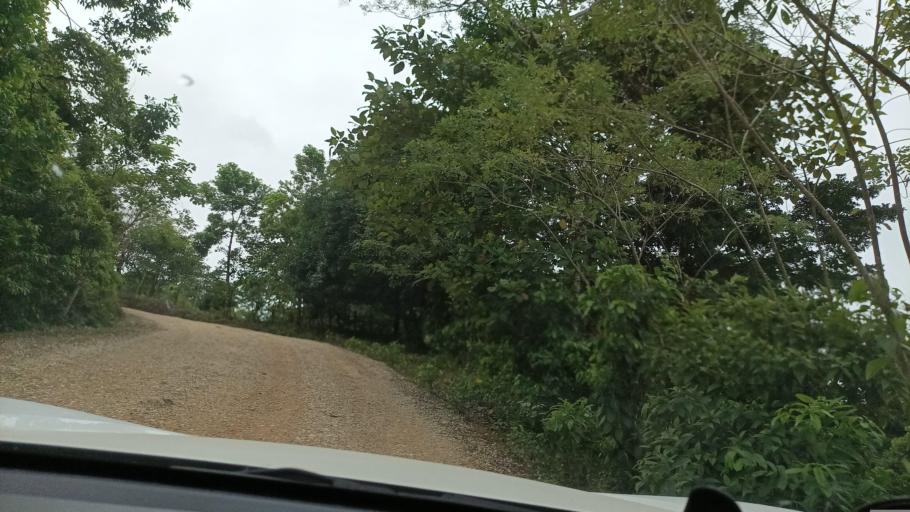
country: MX
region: Veracruz
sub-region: Uxpanapa
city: Poblado 10
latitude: 17.5736
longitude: -94.4231
